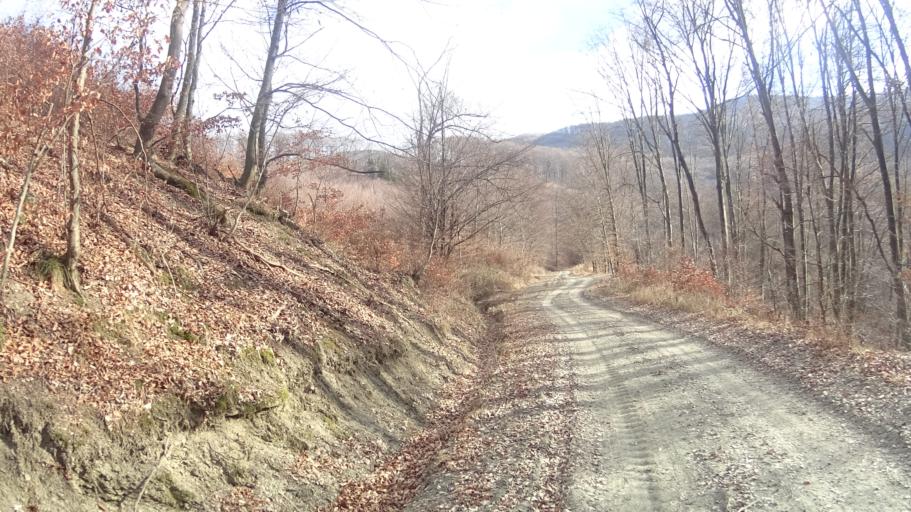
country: HU
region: Heves
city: Szilvasvarad
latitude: 48.0706
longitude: 20.4064
